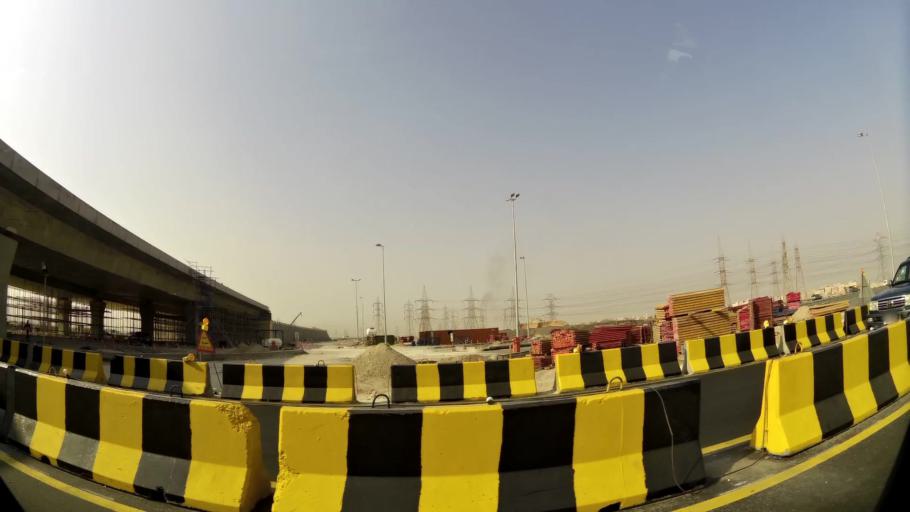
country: KW
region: Muhafazat al Jahra'
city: Al Jahra'
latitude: 29.3364
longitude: 47.7978
